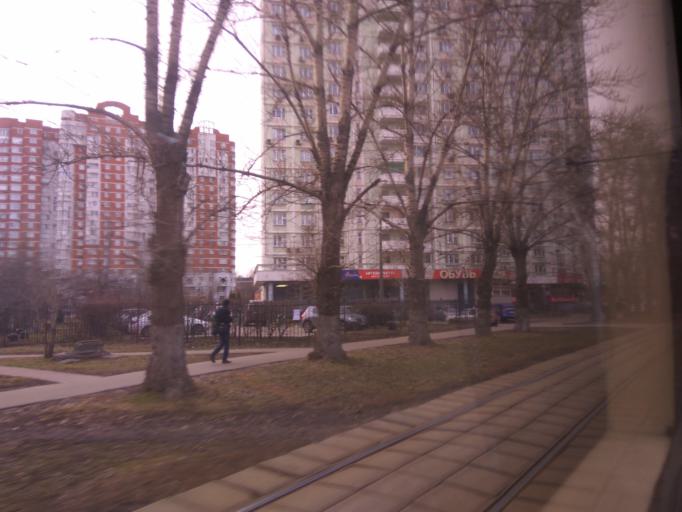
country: RU
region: Moscow
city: Leonovo
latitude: 55.8575
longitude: 37.6600
